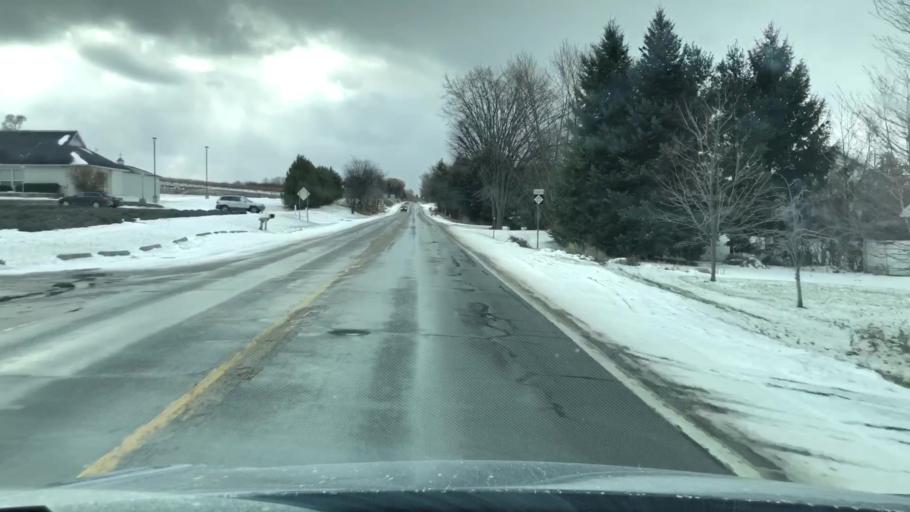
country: US
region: Michigan
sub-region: Antrim County
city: Elk Rapids
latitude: 44.8838
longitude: -85.5154
